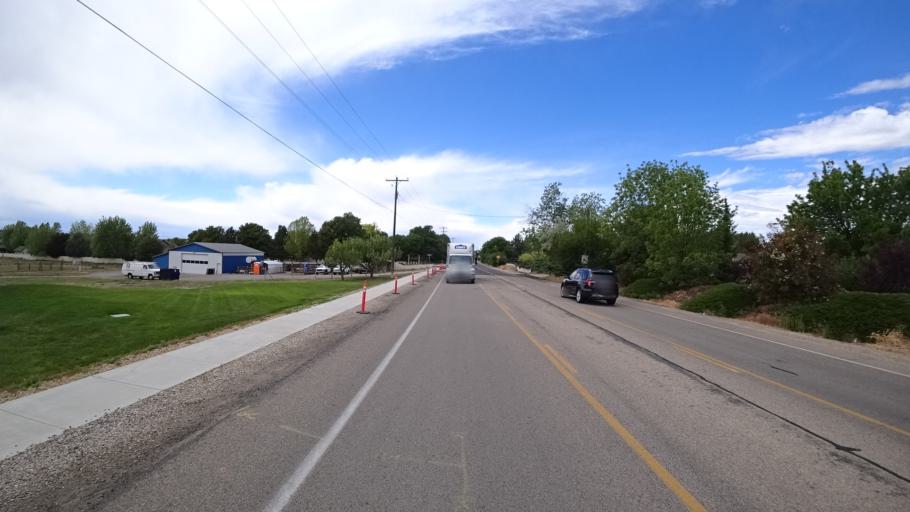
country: US
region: Idaho
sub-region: Ada County
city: Meridian
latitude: 43.5757
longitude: -116.3561
